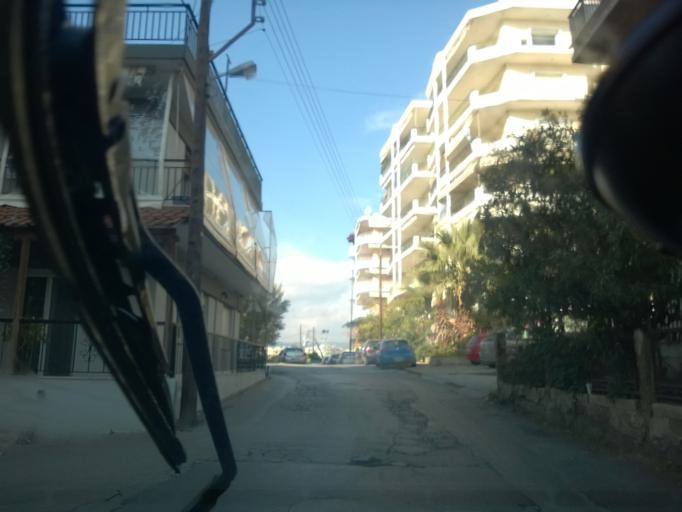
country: GR
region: Central Macedonia
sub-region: Nomos Thessalonikis
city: Stavroupoli
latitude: 40.6714
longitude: 22.9240
